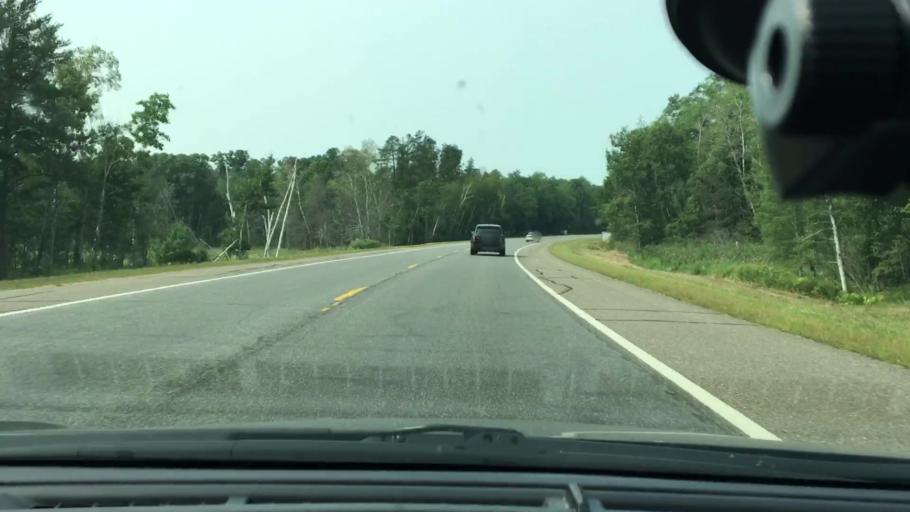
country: US
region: Minnesota
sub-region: Crow Wing County
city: Breezy Point
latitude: 46.4829
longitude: -94.1661
